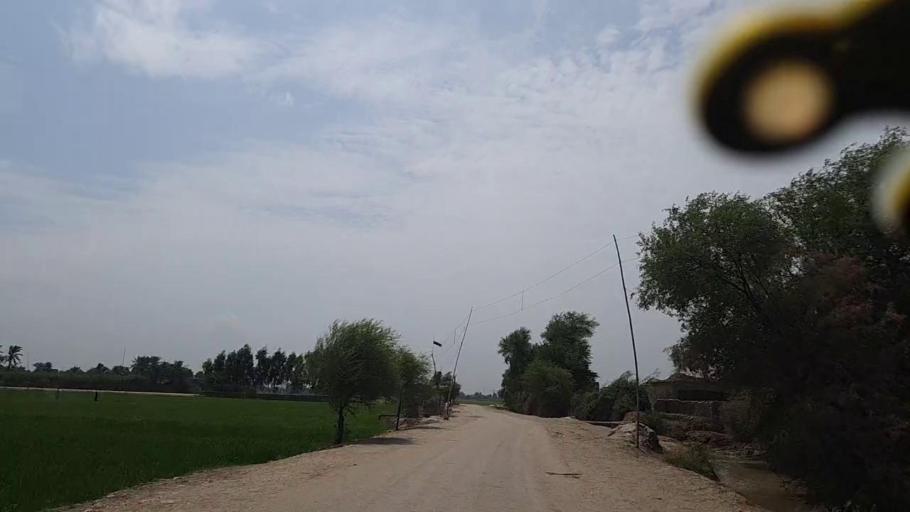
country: PK
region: Sindh
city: Thul
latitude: 28.1123
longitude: 68.8605
